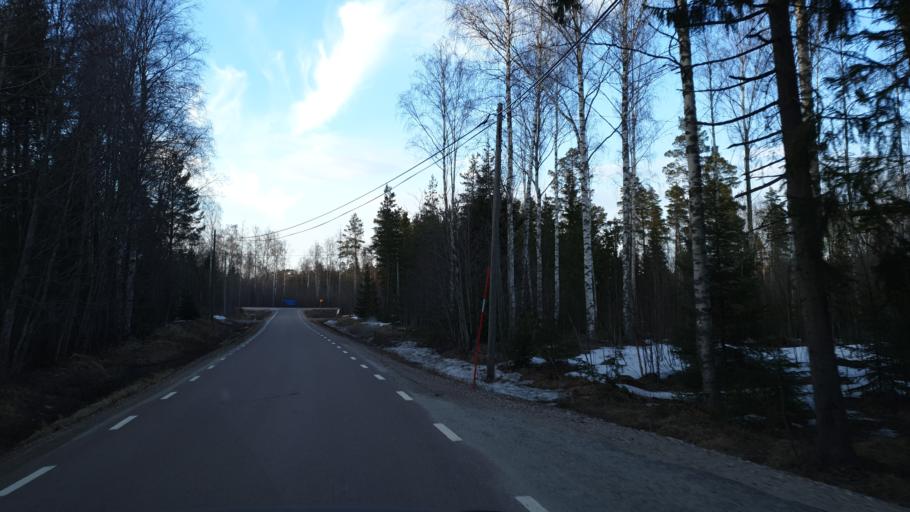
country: SE
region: Vaesternorrland
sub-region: Sundsvalls Kommun
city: Njurundabommen
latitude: 62.2401
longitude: 17.5251
